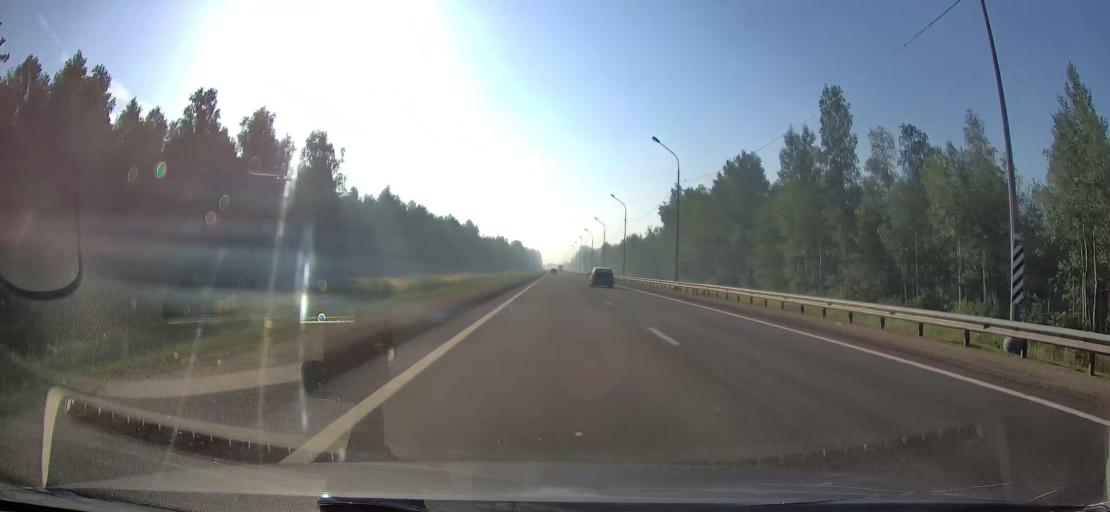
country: RU
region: Leningrad
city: Sinyavino
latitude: 59.8932
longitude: 31.1382
